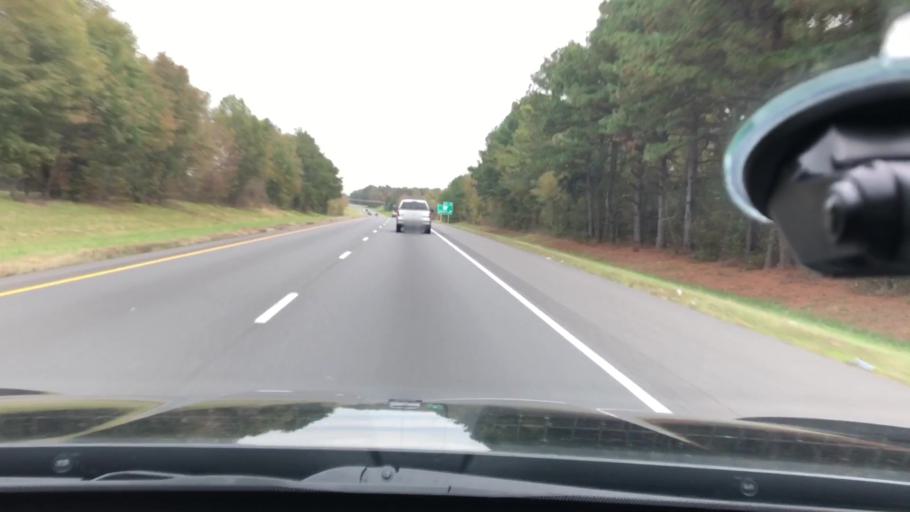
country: US
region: Arkansas
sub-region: Hempstead County
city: Hope
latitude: 33.7331
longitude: -93.5300
